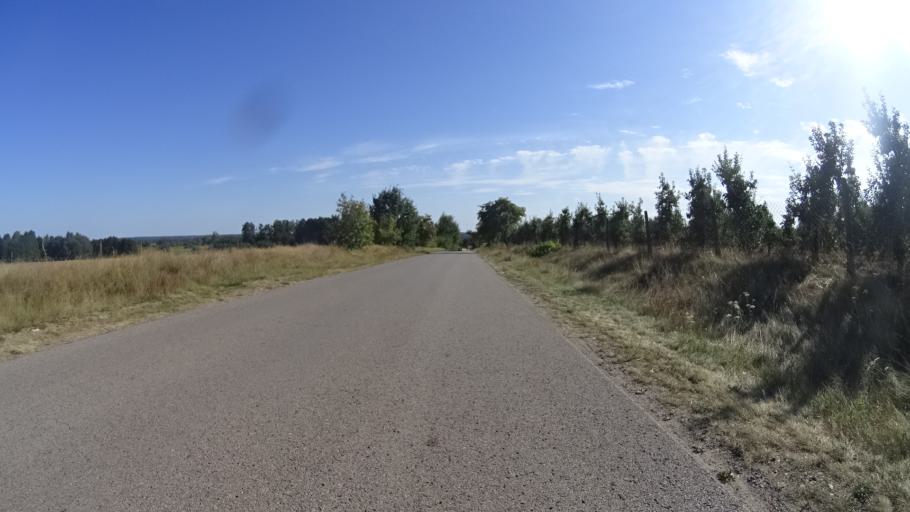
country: PL
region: Masovian Voivodeship
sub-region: Powiat bialobrzeski
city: Wysmierzyce
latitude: 51.6638
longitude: 20.8311
